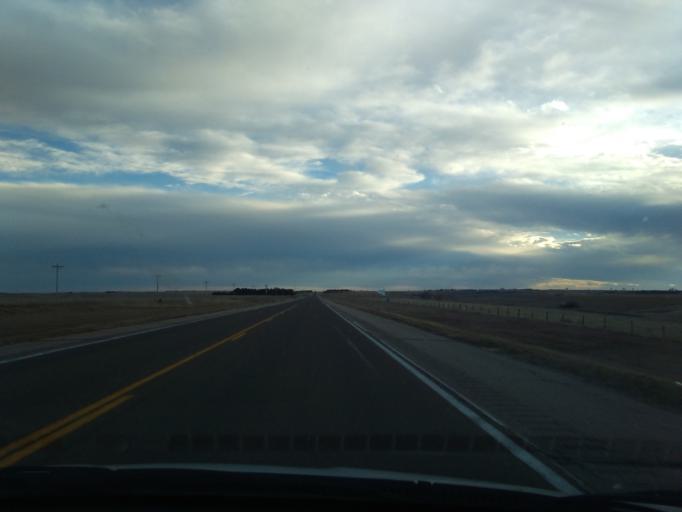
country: US
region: Nebraska
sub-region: Phelps County
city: Holdrege
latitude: 40.3478
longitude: -99.3688
